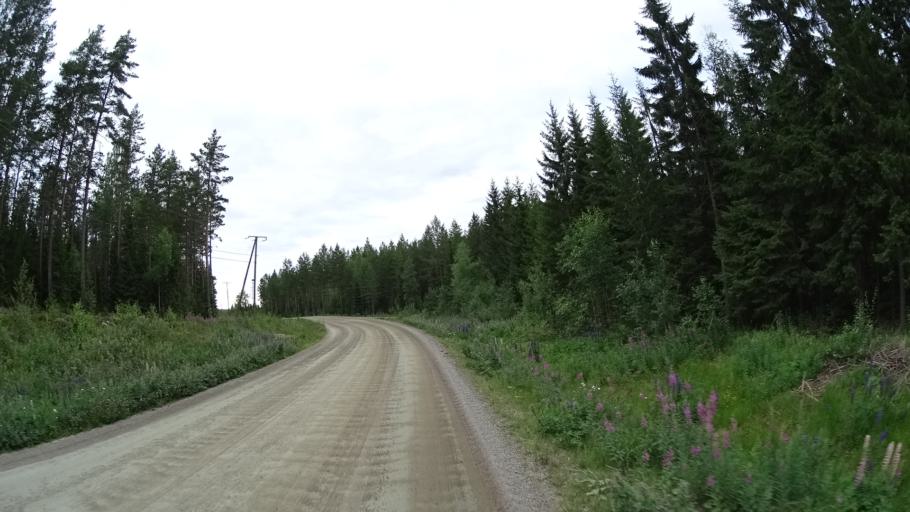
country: FI
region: Satakunta
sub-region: Pohjois-Satakunta
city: Jaemijaervi
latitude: 61.7751
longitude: 22.8624
